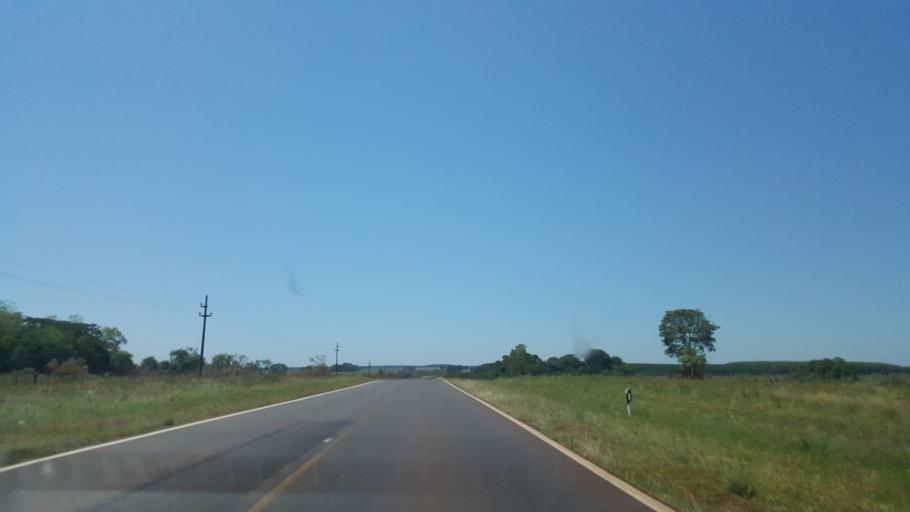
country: AR
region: Corrientes
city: Santo Tome
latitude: -28.3738
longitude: -56.1094
